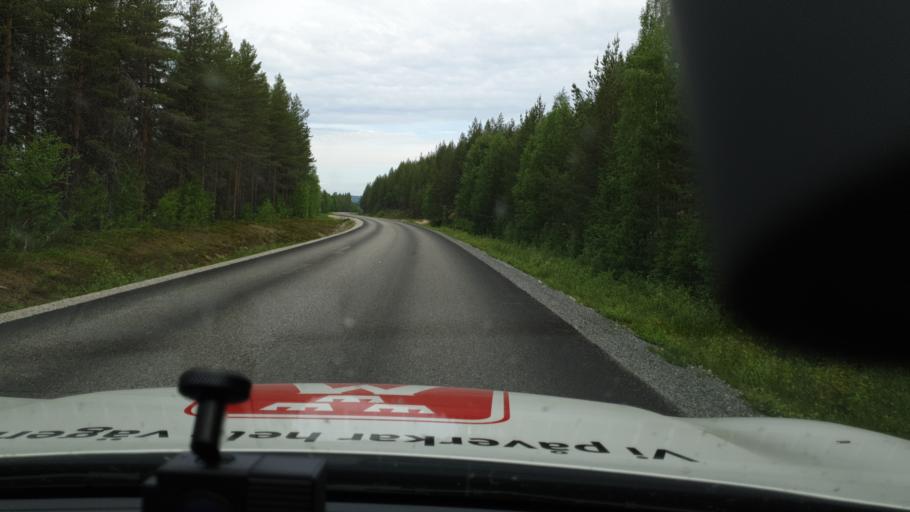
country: SE
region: Vaesterbotten
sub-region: Mala Kommun
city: Mala
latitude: 64.9126
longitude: 18.6567
